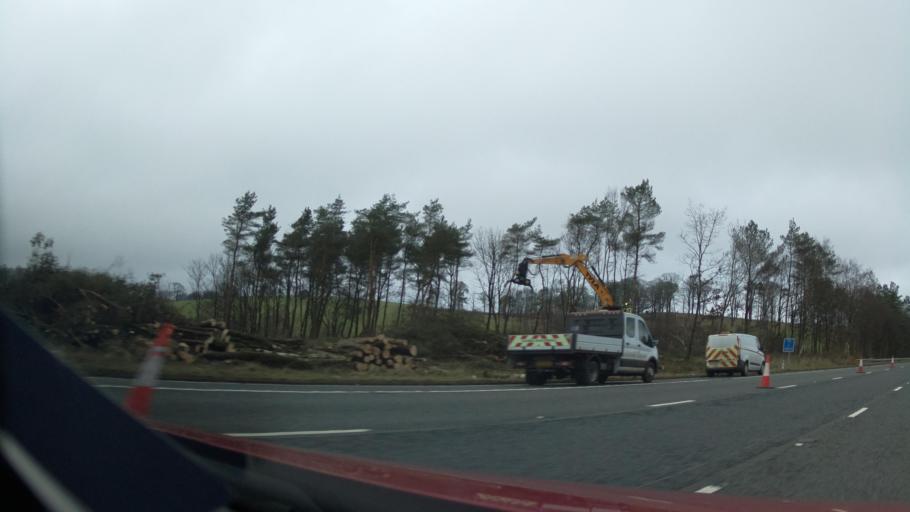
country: GB
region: England
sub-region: Cumbria
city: Sedbergh
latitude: 54.3581
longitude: -2.6139
